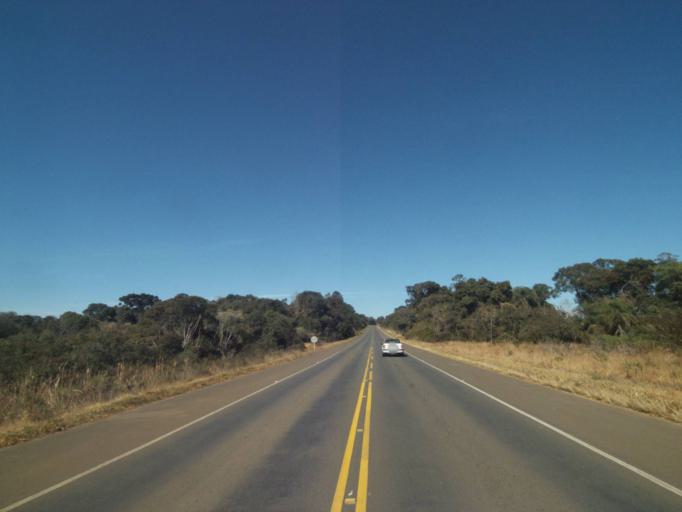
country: BR
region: Parana
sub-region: Tibagi
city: Tibagi
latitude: -24.6560
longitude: -50.4530
